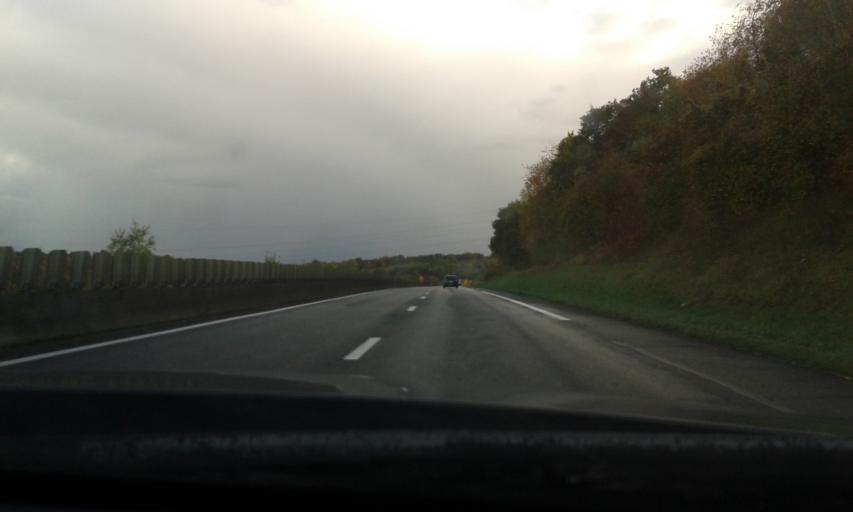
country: FR
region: Haute-Normandie
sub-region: Departement de l'Eure
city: Gravigny
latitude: 49.0445
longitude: 1.1828
